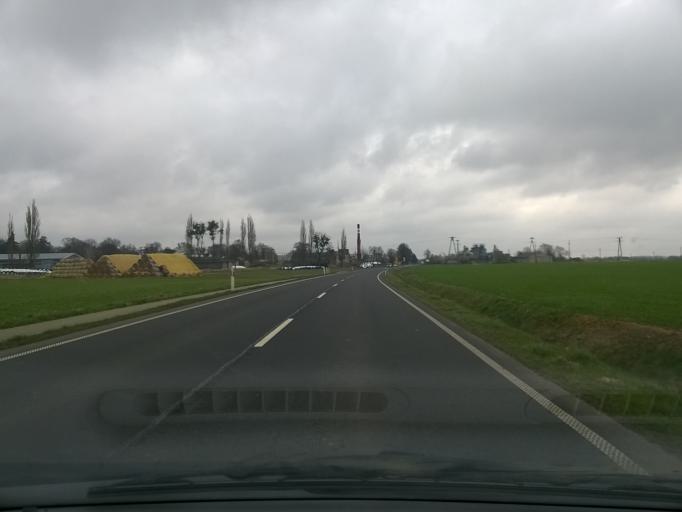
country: PL
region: Kujawsko-Pomorskie
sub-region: Powiat nakielski
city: Kcynia
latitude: 52.9897
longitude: 17.5904
